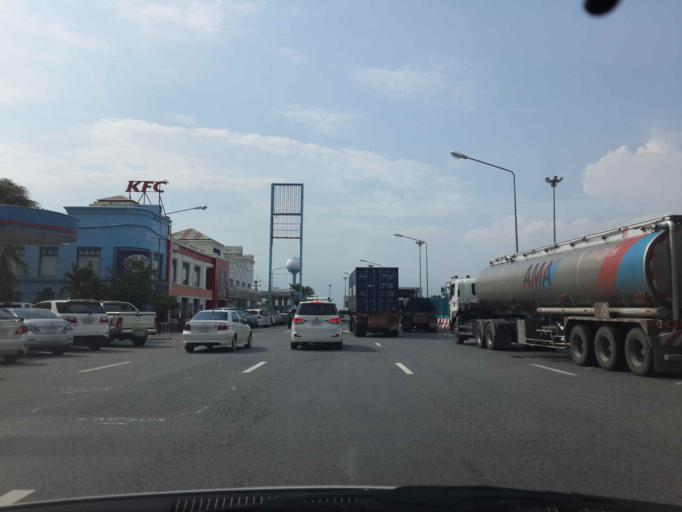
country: TH
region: Chachoengsao
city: Bang Pakong
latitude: 13.5407
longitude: 101.0070
